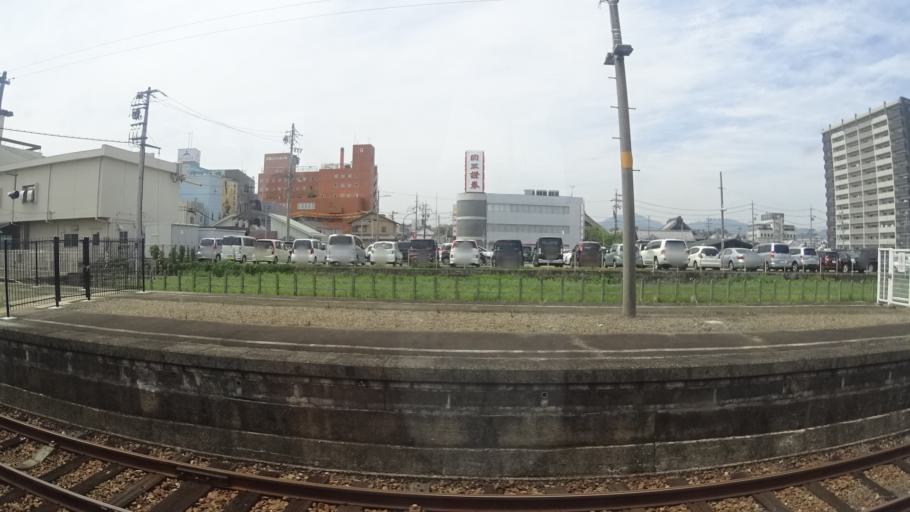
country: JP
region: Mie
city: Hisai-motomachi
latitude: 34.5774
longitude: 136.5355
